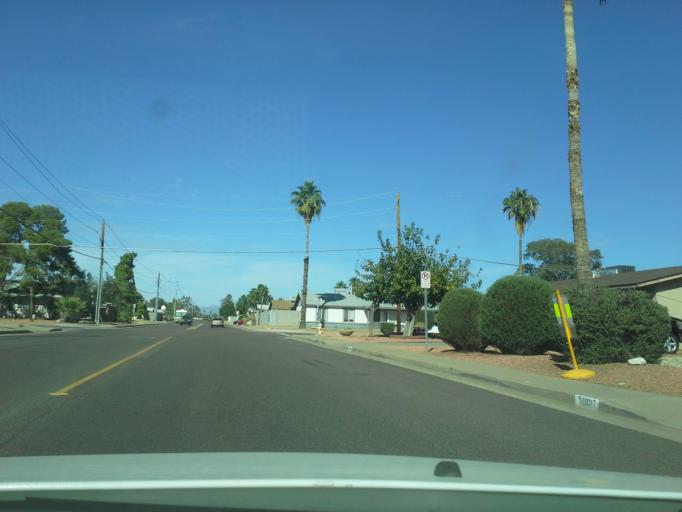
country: US
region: Arizona
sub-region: Maricopa County
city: Paradise Valley
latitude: 33.6222
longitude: -112.0046
